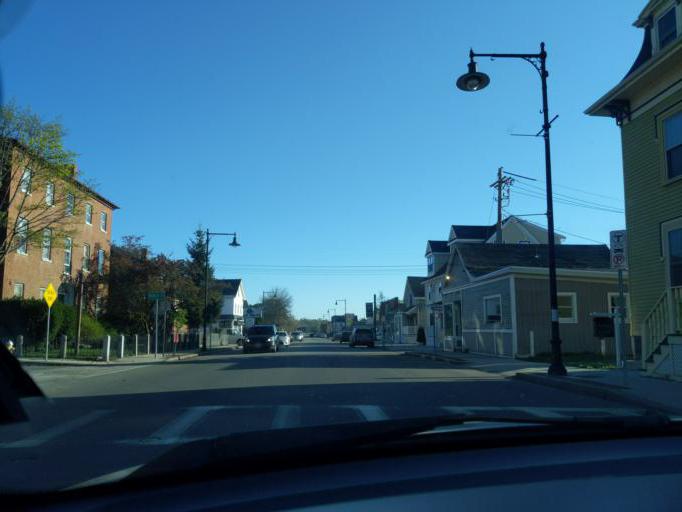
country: US
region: Massachusetts
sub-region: Essex County
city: Salem
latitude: 42.5324
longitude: -70.8884
